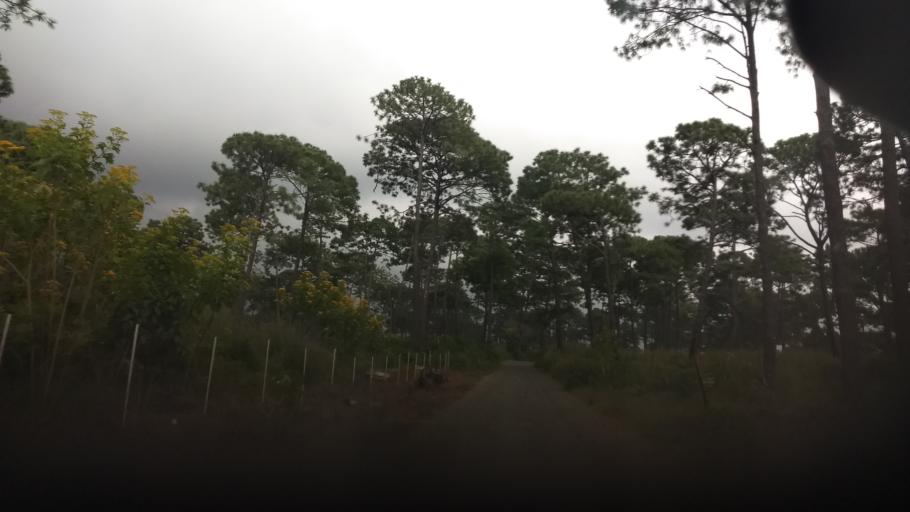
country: MX
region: Jalisco
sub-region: Tonila
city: San Marcos
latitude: 19.4642
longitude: -103.5281
